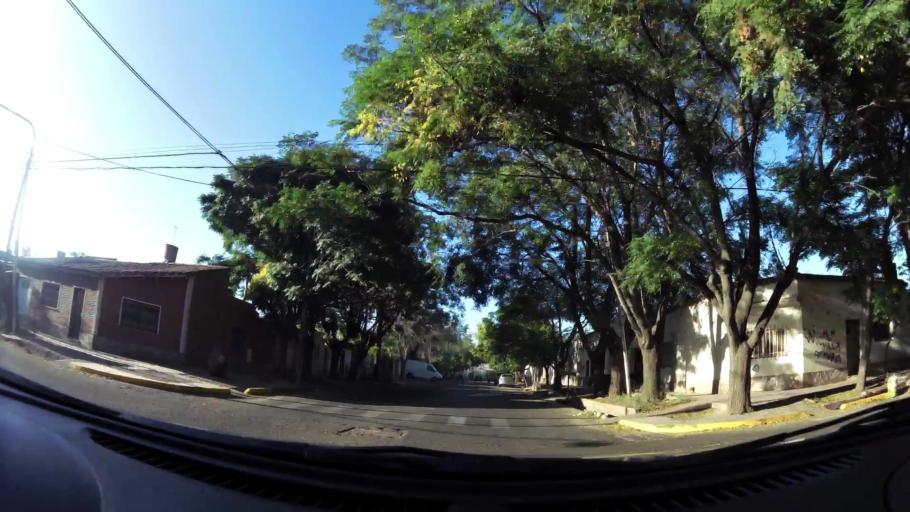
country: AR
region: Mendoza
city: Las Heras
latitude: -32.8653
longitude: -68.8260
